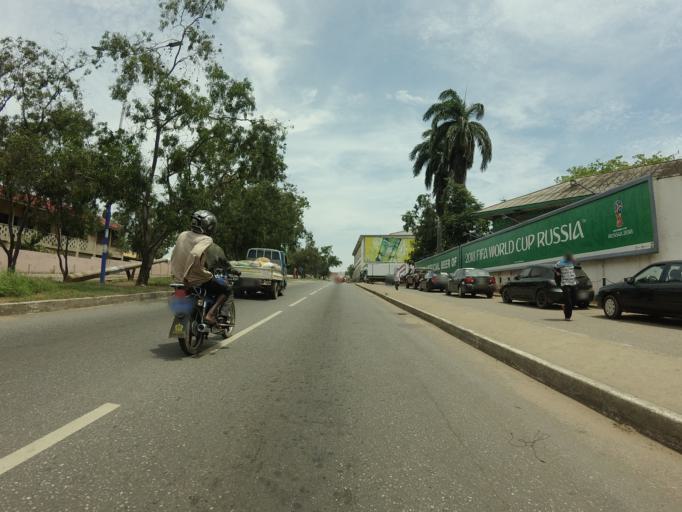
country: GH
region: Greater Accra
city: Accra
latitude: 5.5548
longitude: -0.2168
